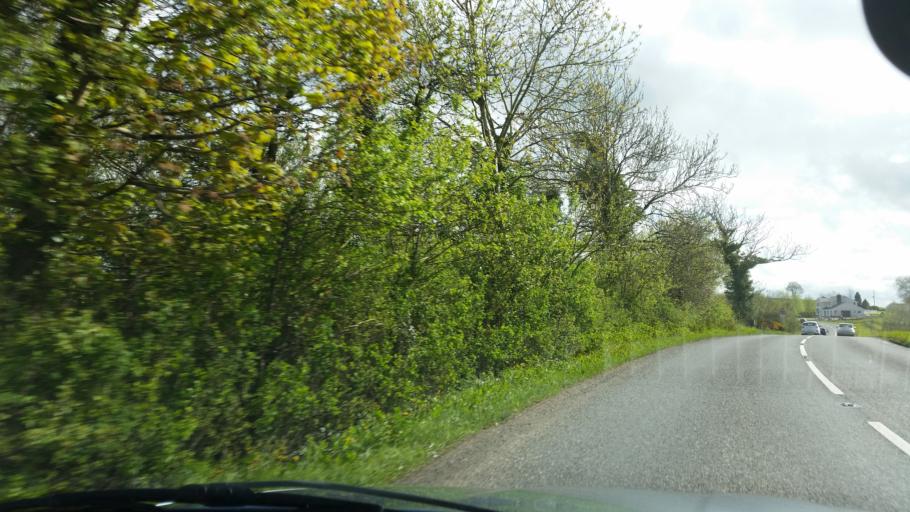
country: GB
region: Northern Ireland
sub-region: Omagh District
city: Omagh
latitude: 54.5686
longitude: -7.2771
